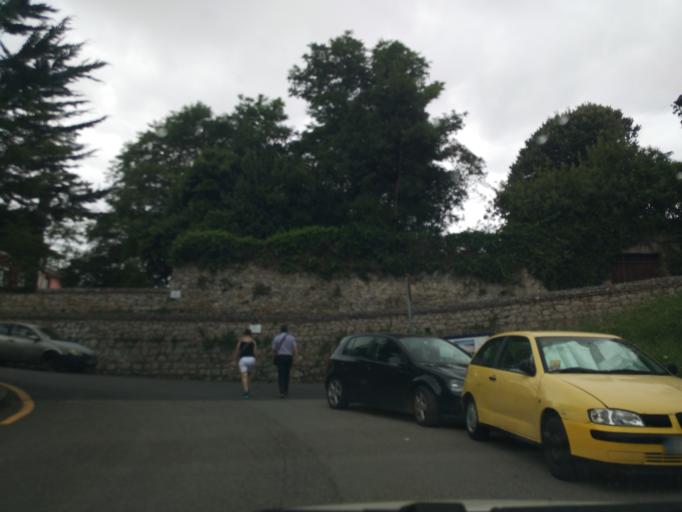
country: ES
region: Cantabria
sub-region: Provincia de Cantabria
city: Comillas
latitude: 43.3873
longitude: -4.2878
